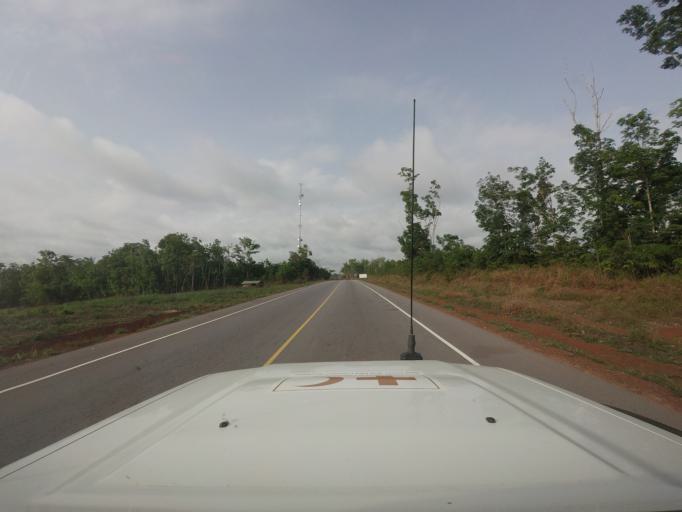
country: LR
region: Bong
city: Gbarnga
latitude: 7.0075
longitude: -9.2840
